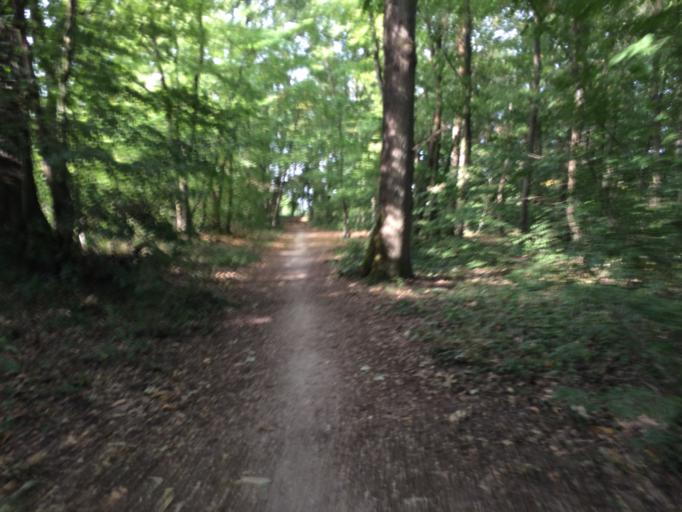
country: FR
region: Ile-de-France
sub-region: Departement de l'Essonne
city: Orsay
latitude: 48.7111
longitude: 2.1929
